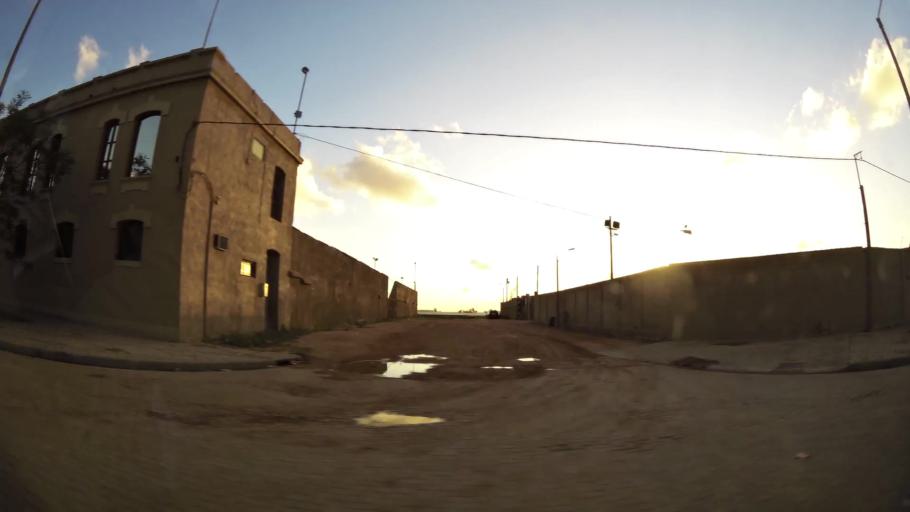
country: UY
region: Montevideo
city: Montevideo
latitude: -34.8800
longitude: -56.2033
